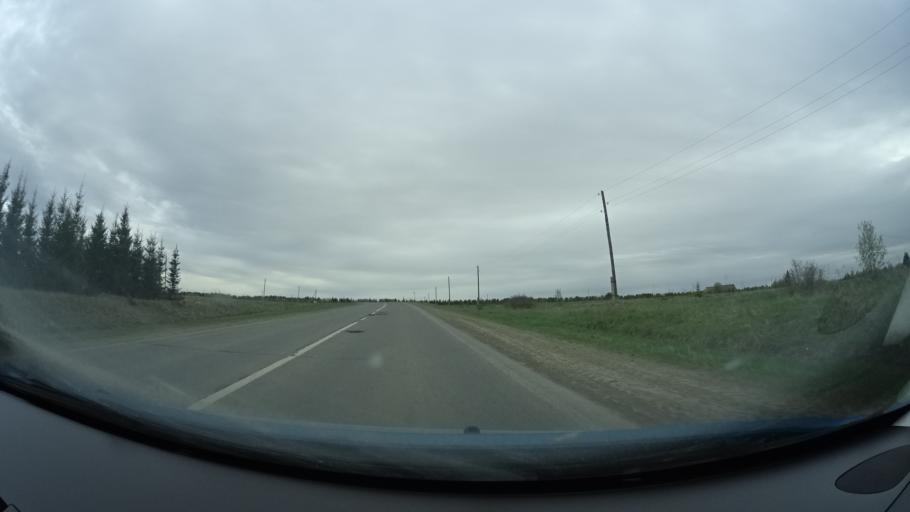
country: RU
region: Perm
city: Osa
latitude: 57.2850
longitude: 55.5687
